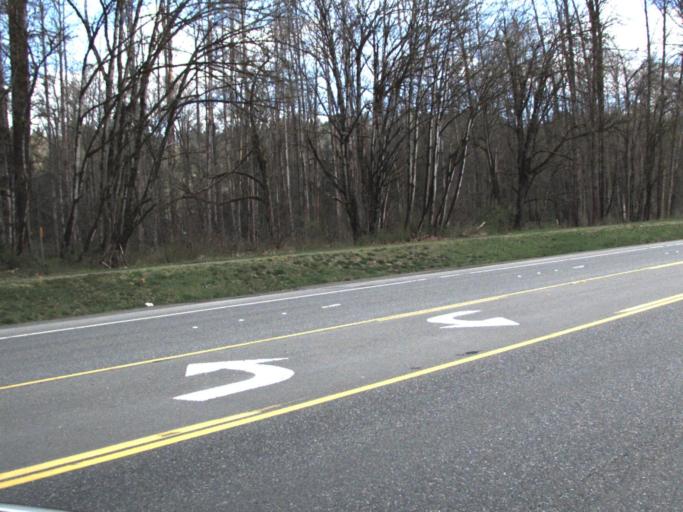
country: US
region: Washington
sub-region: King County
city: Maple Heights-Lake Desire
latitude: 47.4623
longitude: -122.0963
